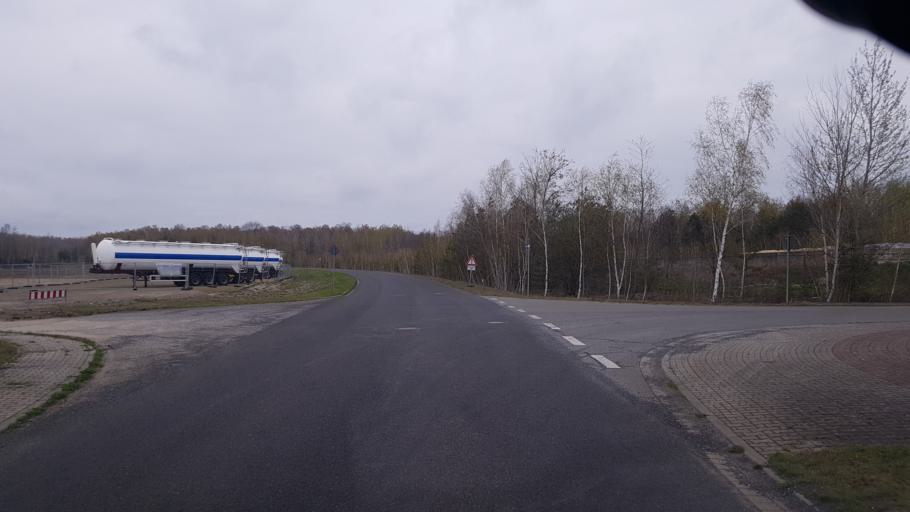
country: DE
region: Brandenburg
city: Lauchhammer
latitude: 51.4802
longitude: 13.7938
